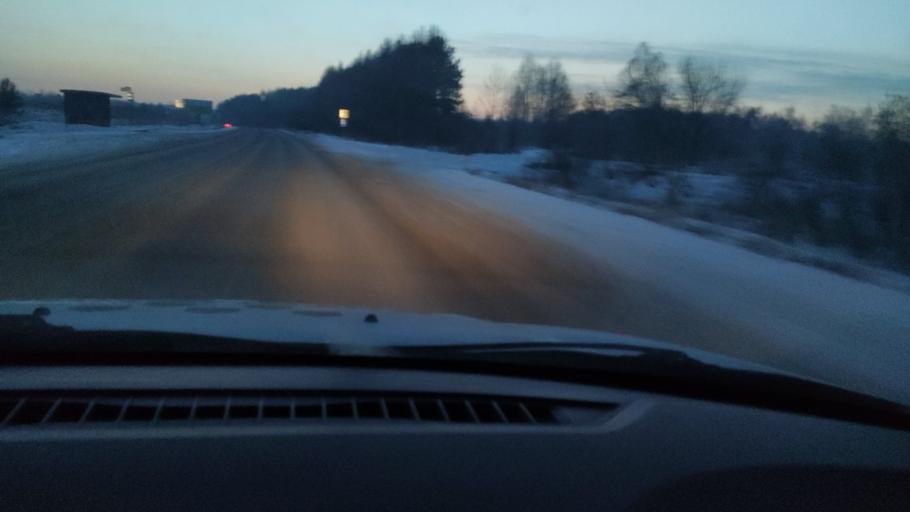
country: RU
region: Perm
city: Kungur
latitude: 57.4204
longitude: 56.9210
